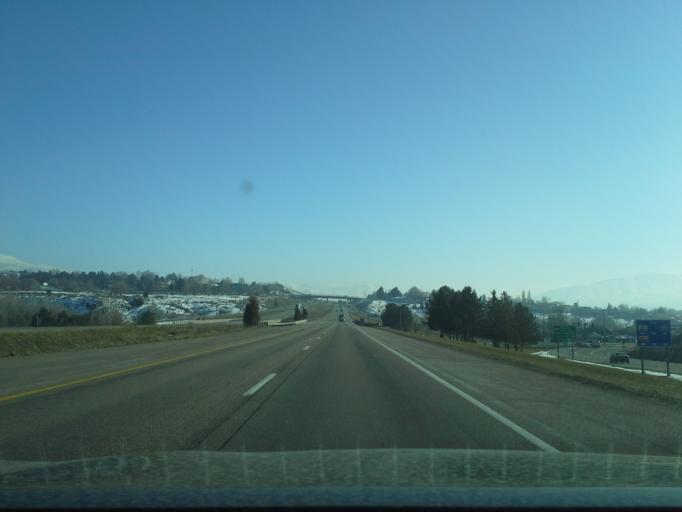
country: US
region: Idaho
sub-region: Bannock County
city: Pocatello
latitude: 42.8993
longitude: -112.4367
